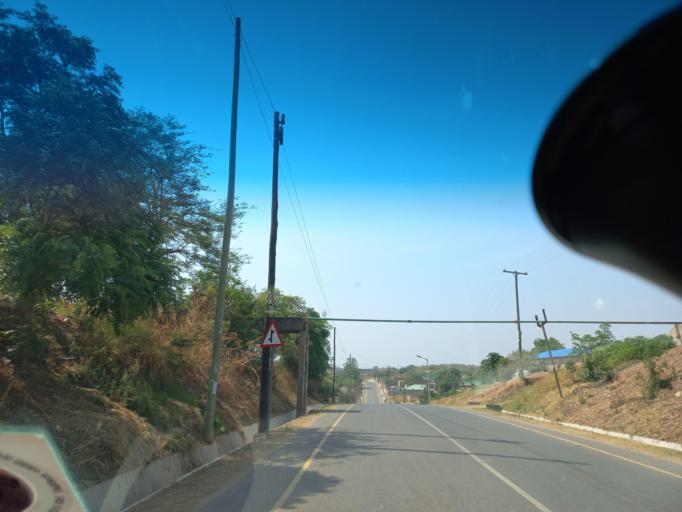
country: ZM
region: Lusaka
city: Lusaka
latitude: -15.5670
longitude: 28.2694
